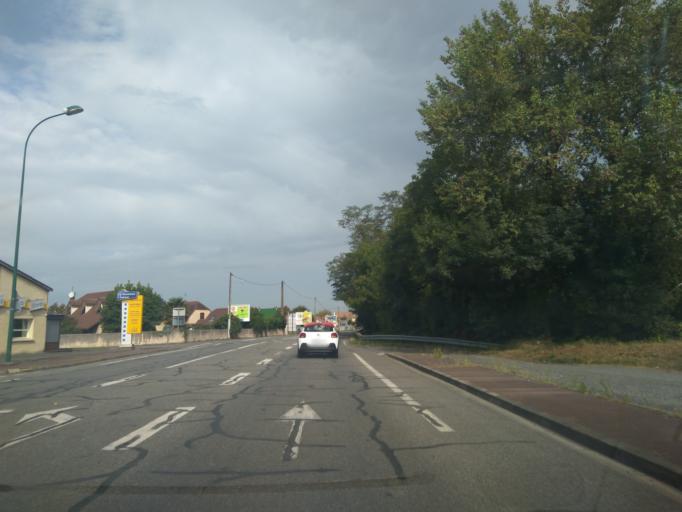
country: FR
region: Aquitaine
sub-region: Departement des Pyrenees-Atlantiques
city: Artiguelouve
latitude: 43.3094
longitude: -0.4483
